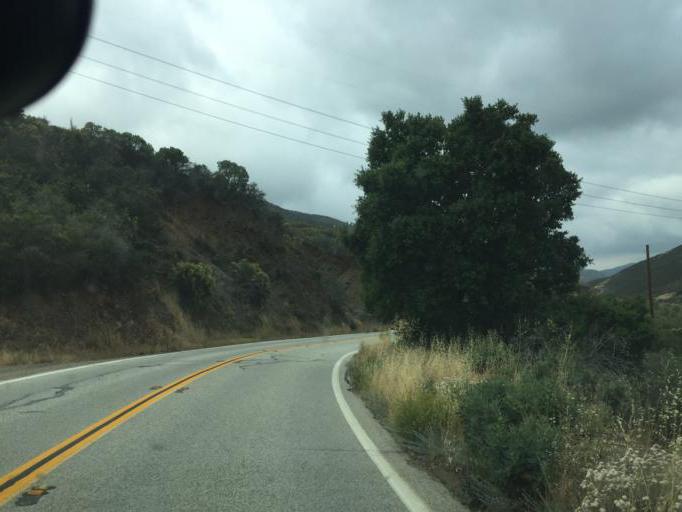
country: US
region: California
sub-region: Los Angeles County
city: Green Valley
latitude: 34.5746
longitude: -118.3852
